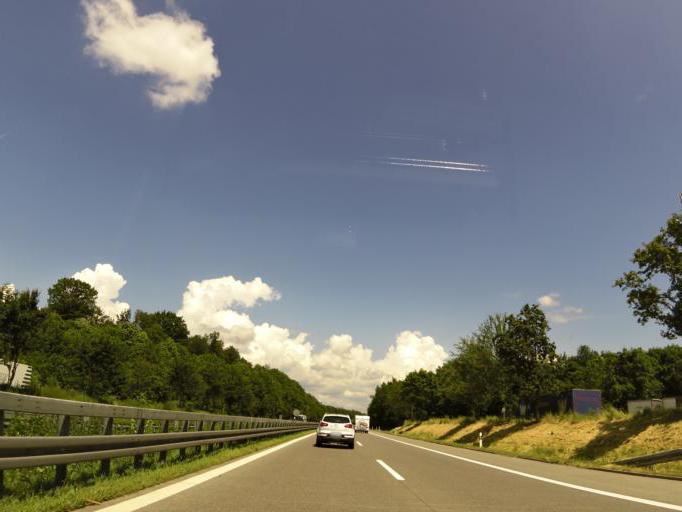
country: DE
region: Baden-Wuerttemberg
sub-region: Tuebingen Region
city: Nerenstetten
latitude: 48.5231
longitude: 10.0828
